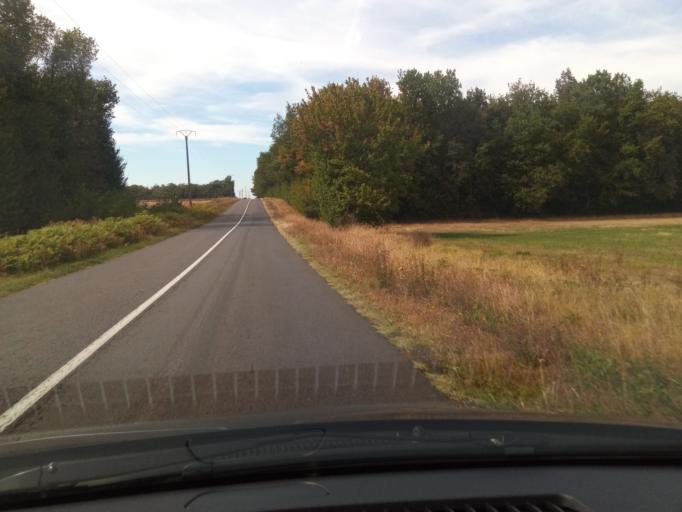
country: FR
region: Poitou-Charentes
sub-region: Departement de la Vienne
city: Chauvigny
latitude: 46.5209
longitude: 0.7446
